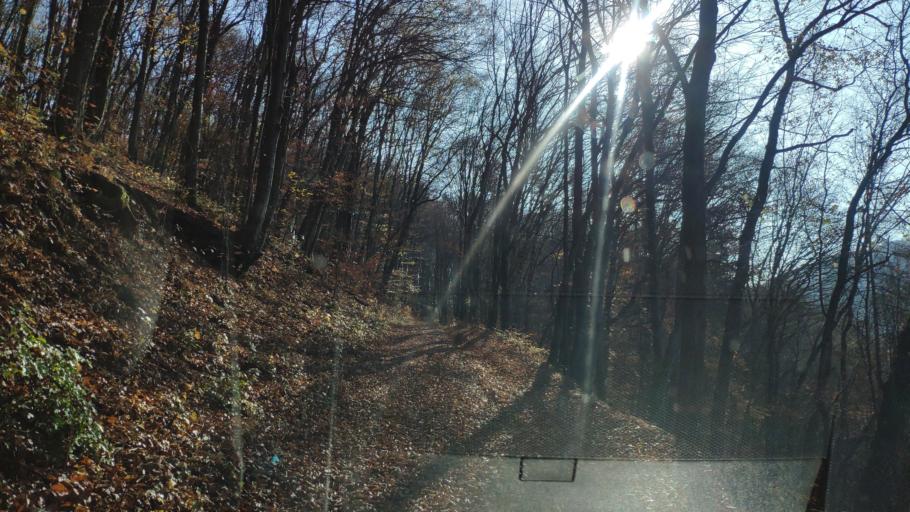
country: SK
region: Presovsky
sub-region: Okres Presov
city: Presov
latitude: 48.8972
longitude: 21.2079
